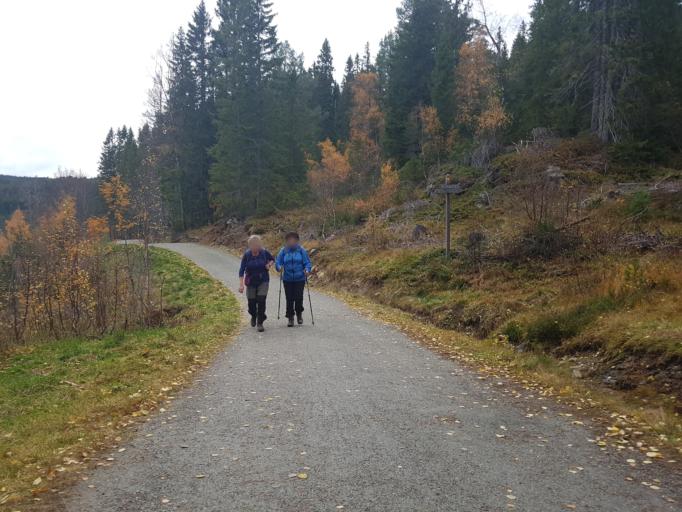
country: NO
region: Sor-Trondelag
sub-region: Melhus
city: Melhus
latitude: 63.4017
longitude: 10.2486
